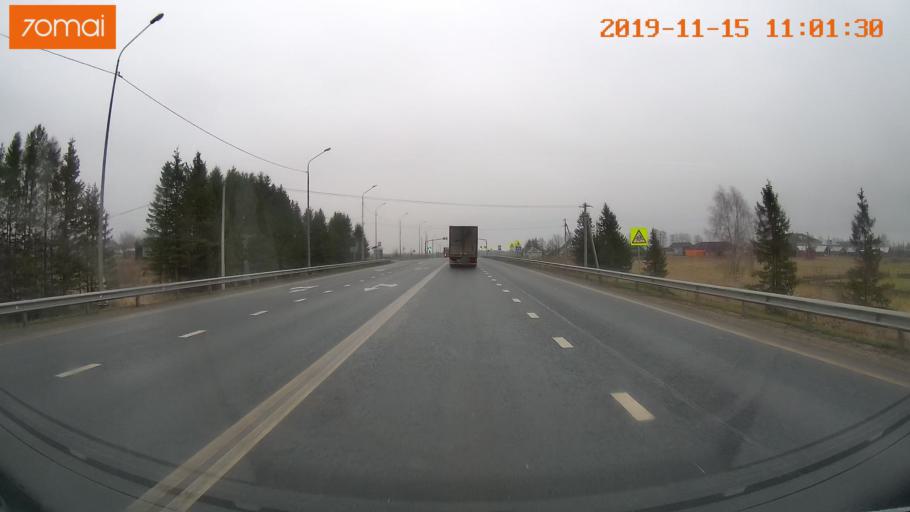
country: RU
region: Vologda
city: Chebsara
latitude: 59.1325
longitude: 38.9224
